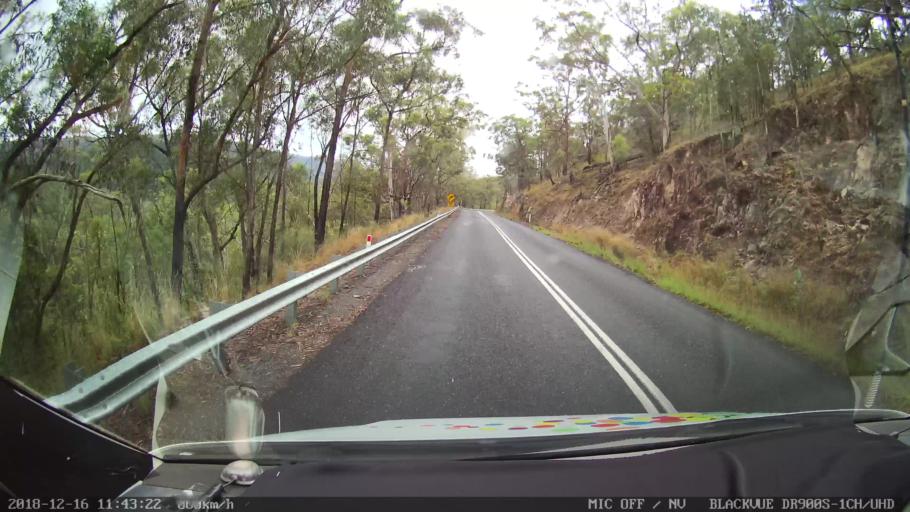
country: AU
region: New South Wales
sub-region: Tenterfield Municipality
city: Carrolls Creek
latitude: -28.9459
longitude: 152.2164
